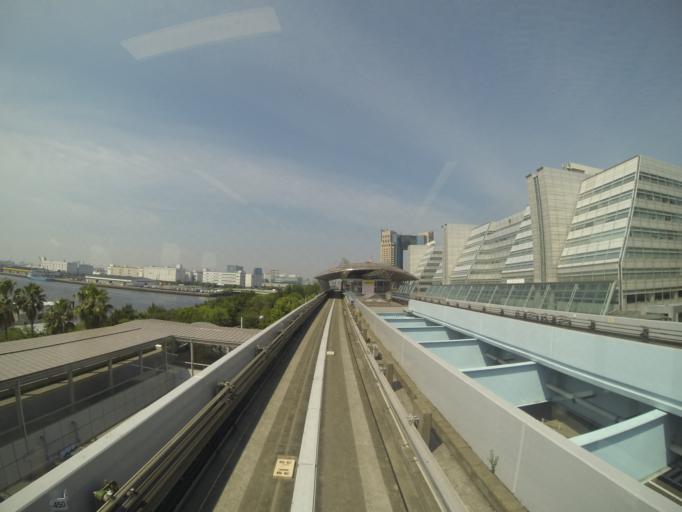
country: JP
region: Tokyo
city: Urayasu
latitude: 35.6307
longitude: 139.7924
